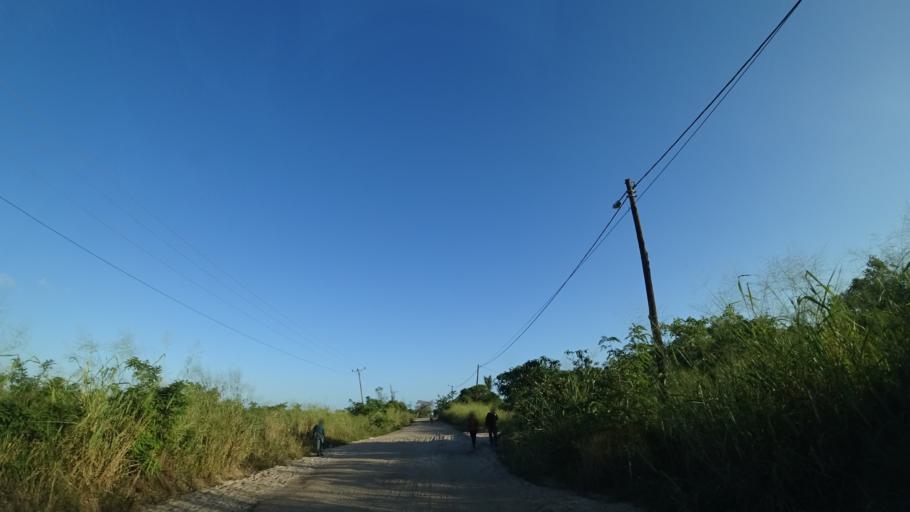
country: MZ
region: Sofala
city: Dondo
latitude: -19.3927
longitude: 34.7086
